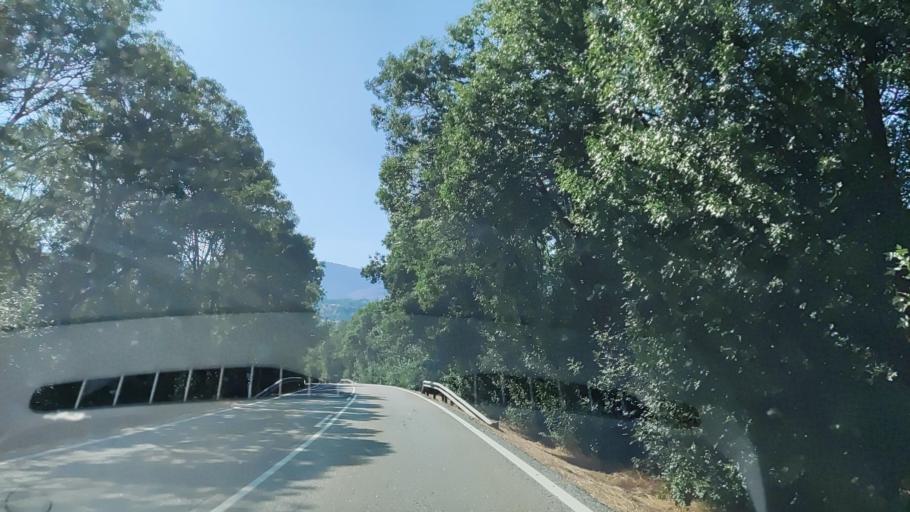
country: ES
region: Madrid
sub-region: Provincia de Madrid
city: Lozoya
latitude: 40.9559
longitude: -3.7788
